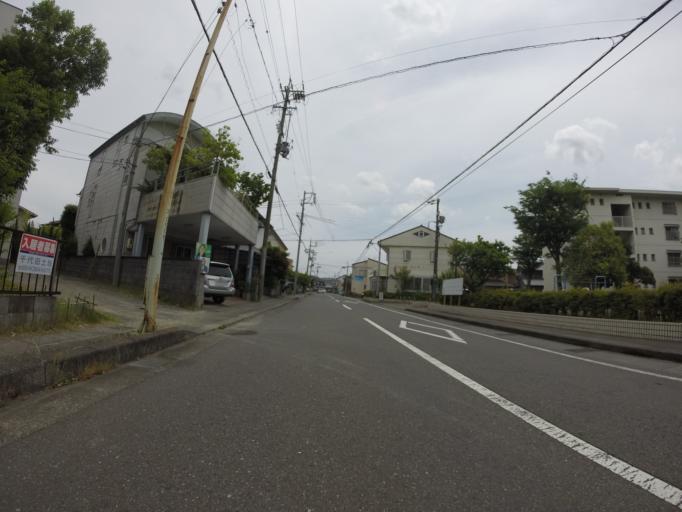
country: JP
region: Shizuoka
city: Shizuoka-shi
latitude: 35.0031
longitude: 138.4098
